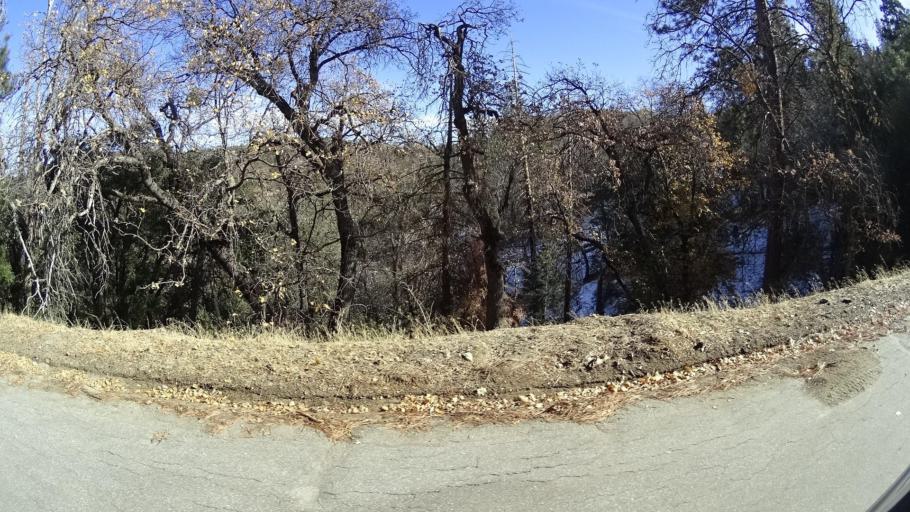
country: US
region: California
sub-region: Kern County
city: Bodfish
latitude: 35.4774
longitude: -118.6402
